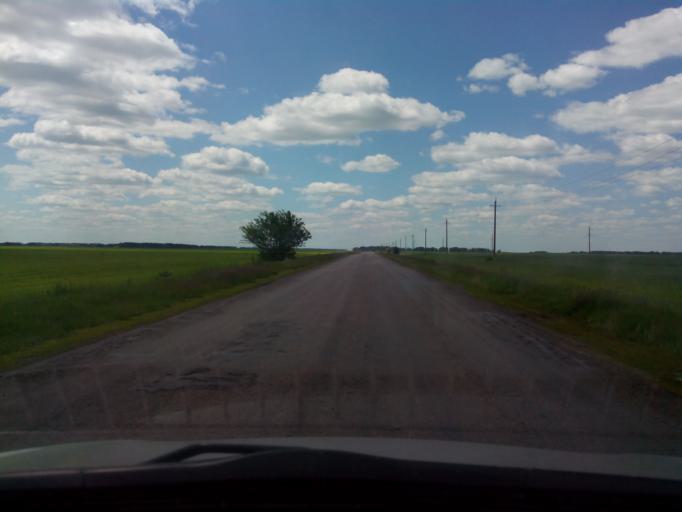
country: RU
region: Voronezj
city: Gribanovskiy
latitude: 51.6234
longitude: 41.8820
